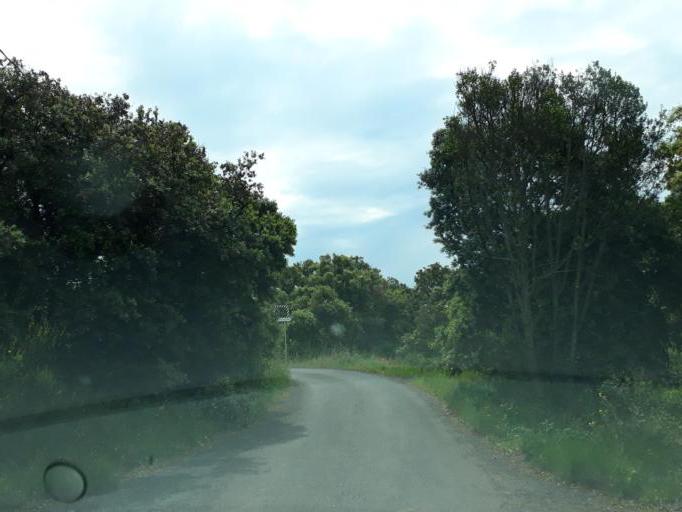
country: FR
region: Languedoc-Roussillon
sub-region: Departement de l'Herault
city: Le Cap d'Agde
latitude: 43.2922
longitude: 3.4929
